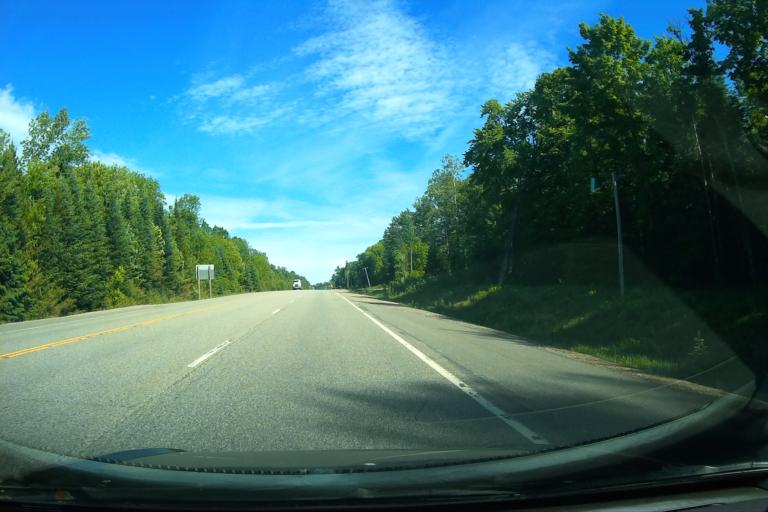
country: CA
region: Ontario
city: Deep River
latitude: 46.1628
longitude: -77.6073
